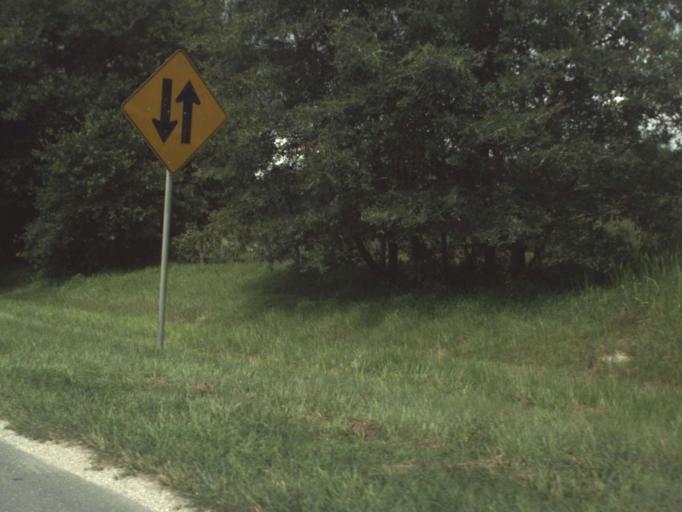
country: US
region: Florida
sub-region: Sumter County
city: Bushnell
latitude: 28.6525
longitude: -82.1177
